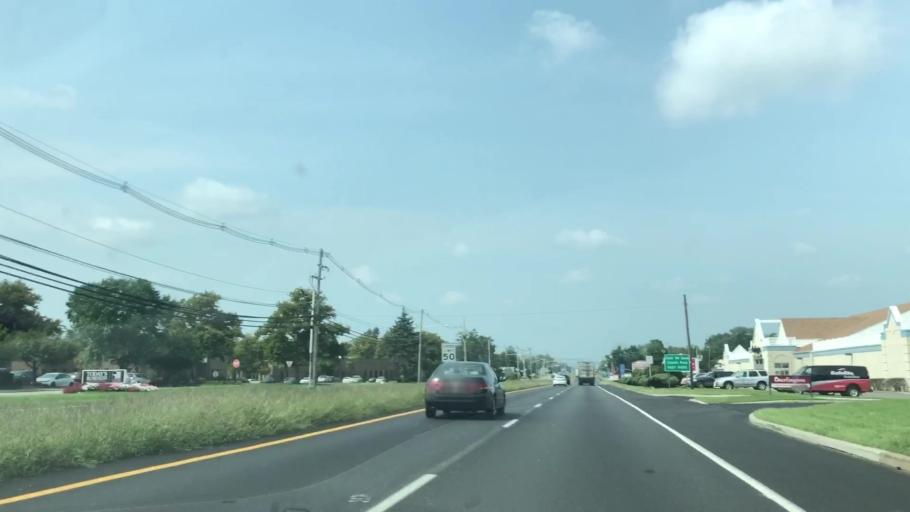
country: US
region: New Jersey
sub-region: Essex County
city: West Caldwell
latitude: 40.8589
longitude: -74.3348
